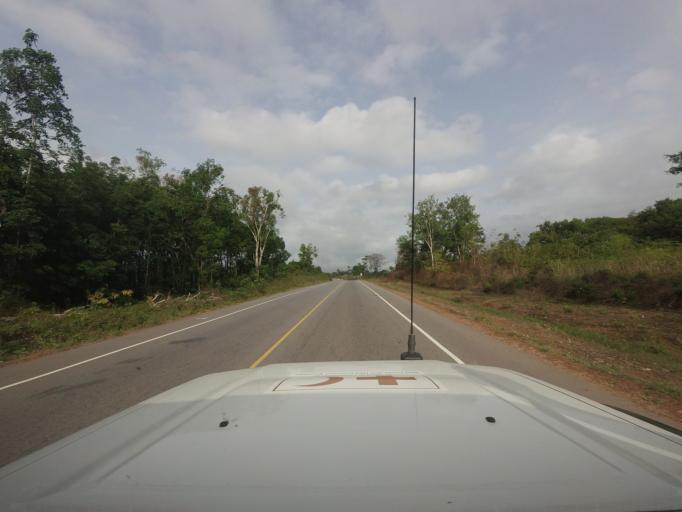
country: LR
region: Bong
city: Gbarnga
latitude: 7.0042
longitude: -9.2988
